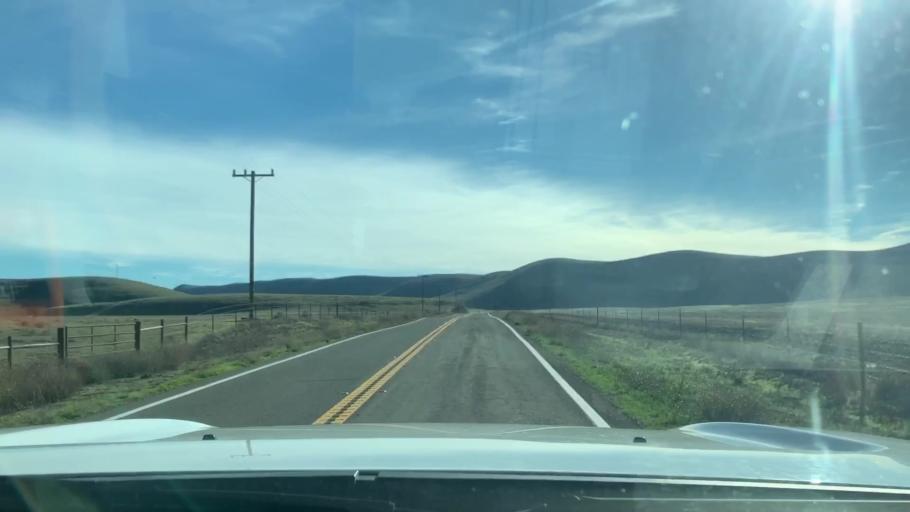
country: US
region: California
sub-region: Monterey County
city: King City
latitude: 36.1501
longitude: -120.9682
